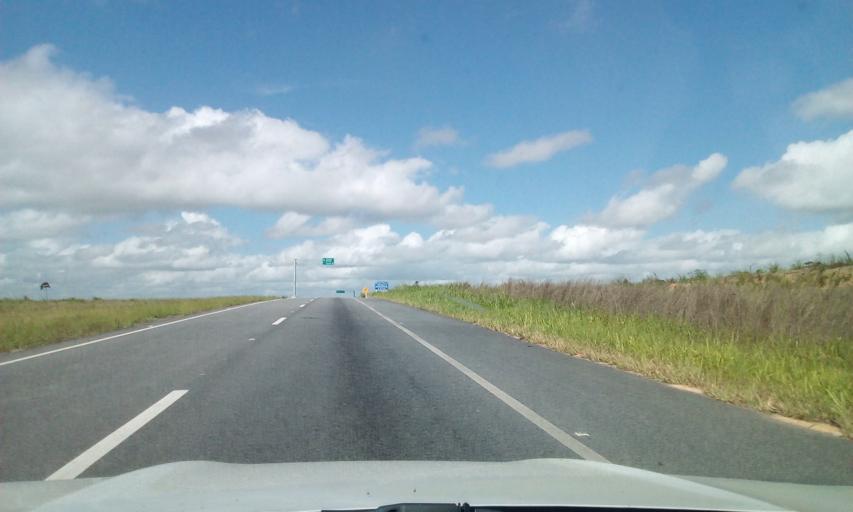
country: BR
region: Alagoas
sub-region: Rio Largo
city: Rio Largo
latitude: -9.4563
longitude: -35.8773
